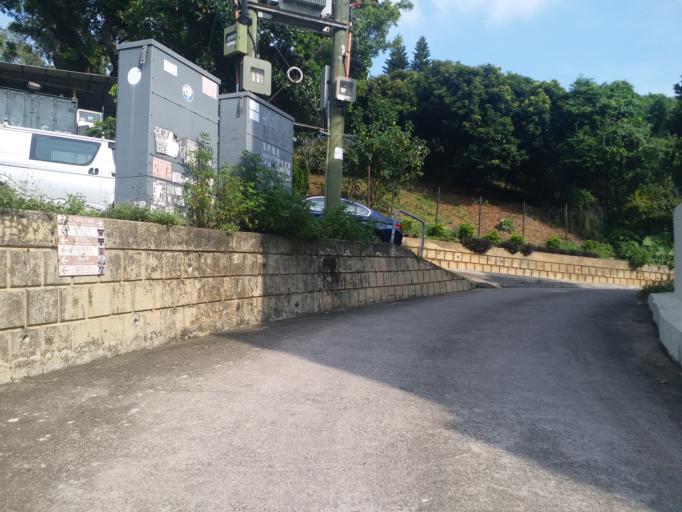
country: HK
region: Yuen Long
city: Yuen Long Kau Hui
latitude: 22.4448
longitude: 114.0091
